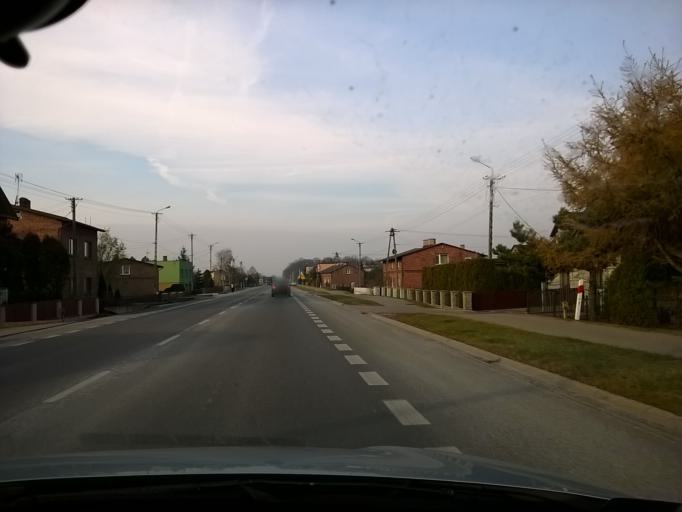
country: PL
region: Silesian Voivodeship
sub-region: Powiat gliwicki
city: Paniowki
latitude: 50.2402
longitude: 18.7677
